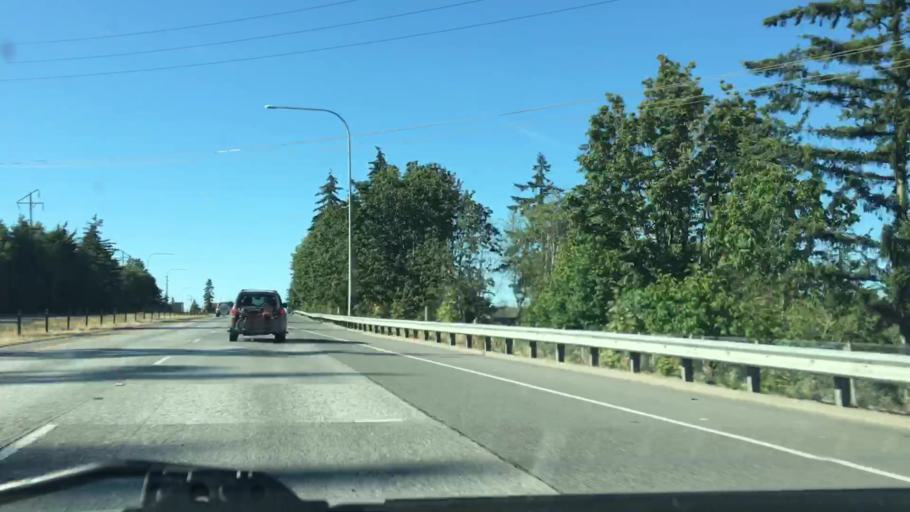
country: US
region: Washington
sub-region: Whatcom County
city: Bellingham
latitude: 48.7377
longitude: -122.4674
